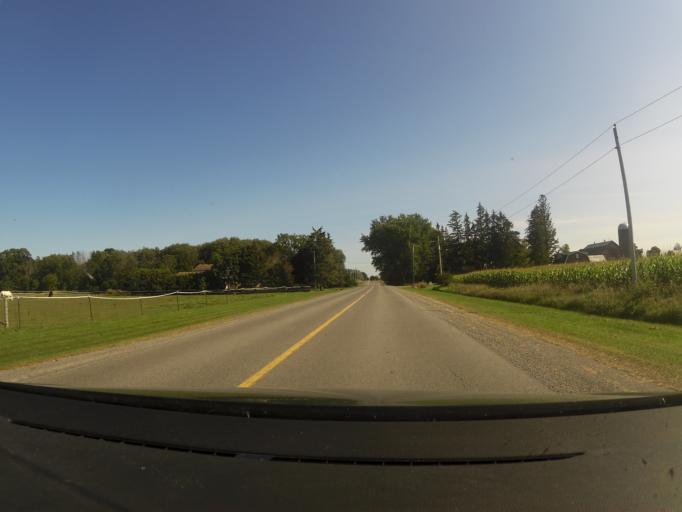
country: CA
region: Ontario
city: Carleton Place
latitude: 45.3490
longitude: -76.0869
